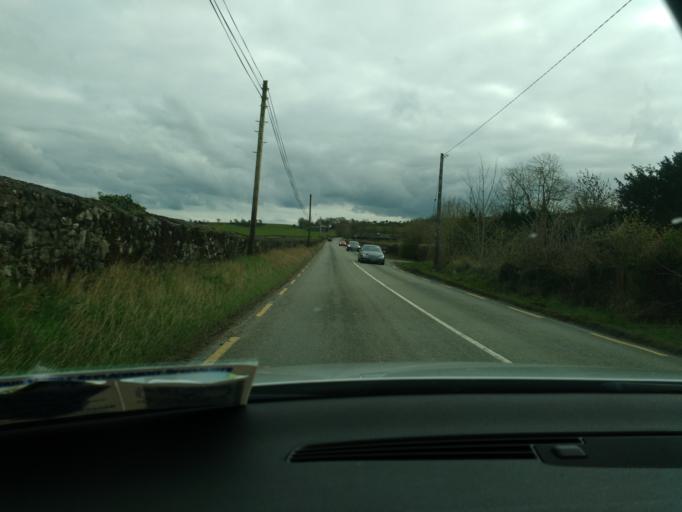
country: IE
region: Leinster
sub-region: Kilkenny
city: Ballyragget
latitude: 52.7069
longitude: -7.3171
